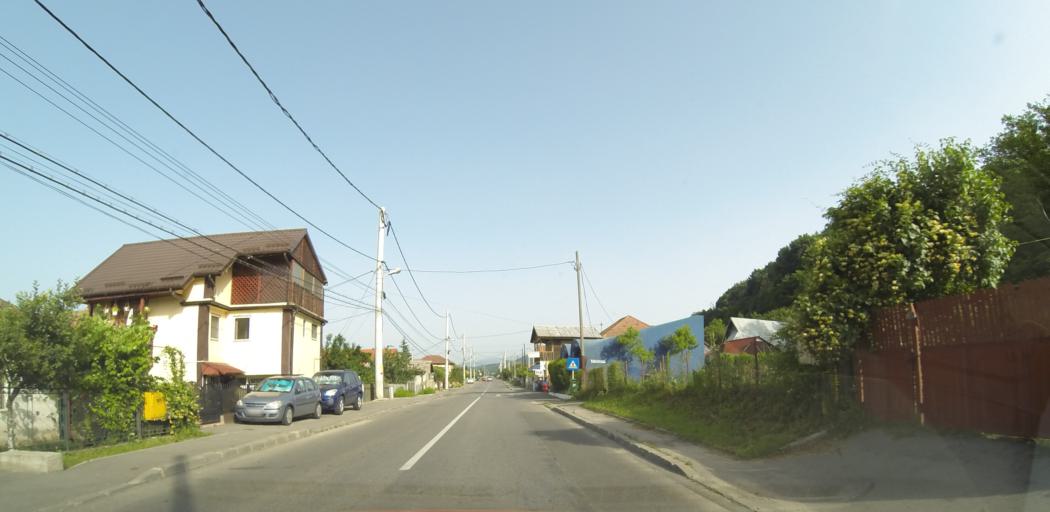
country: RO
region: Valcea
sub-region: Comuna Vladesti
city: Vladesti
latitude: 45.1117
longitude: 24.3259
